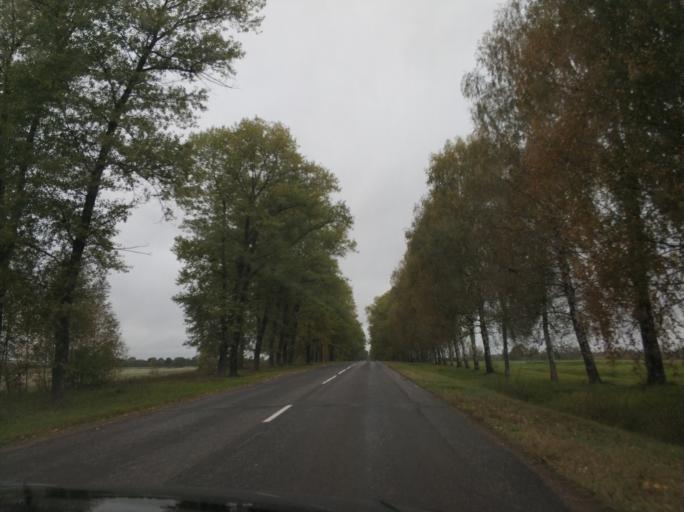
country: BY
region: Vitebsk
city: Polatsk
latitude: 55.4353
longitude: 28.9769
